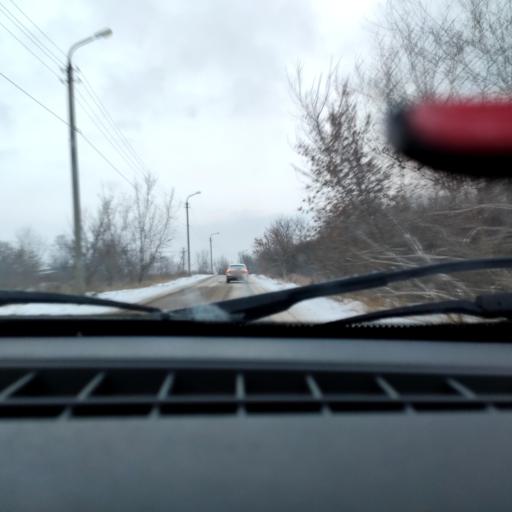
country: RU
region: Bashkortostan
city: Blagoveshchensk
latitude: 54.8908
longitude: 56.0493
